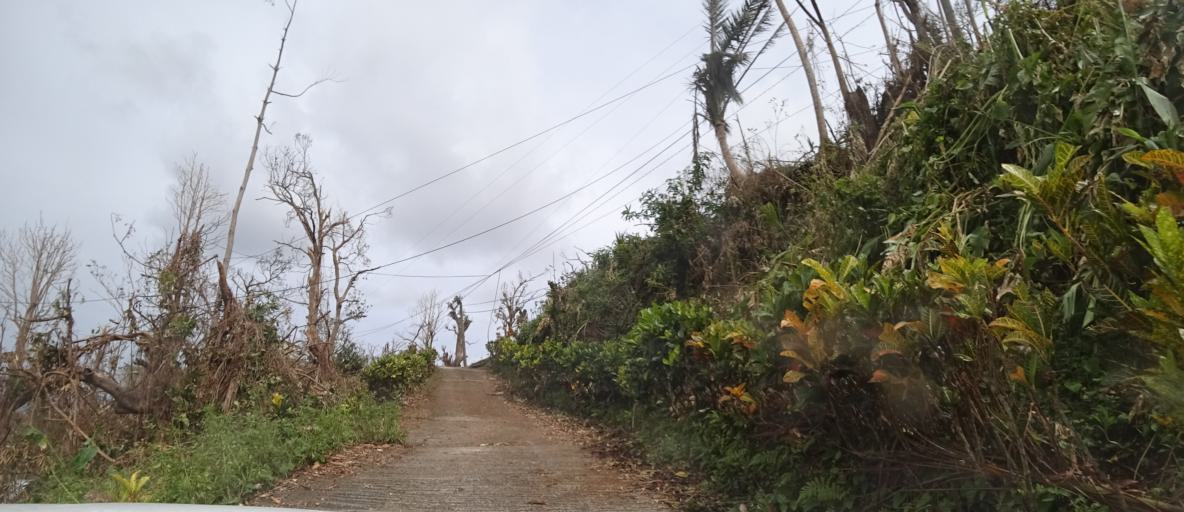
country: DM
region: Saint Andrew
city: Calibishie
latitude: 15.5883
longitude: -61.4045
